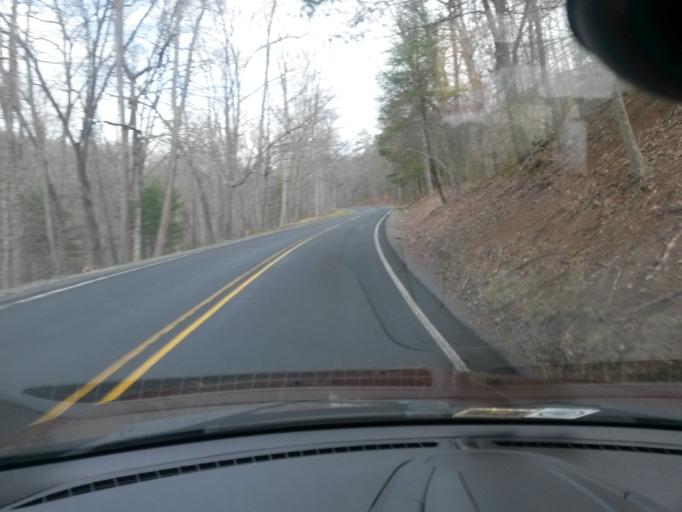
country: US
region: Virginia
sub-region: Bath County
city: Warm Springs
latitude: 38.1211
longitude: -79.7542
